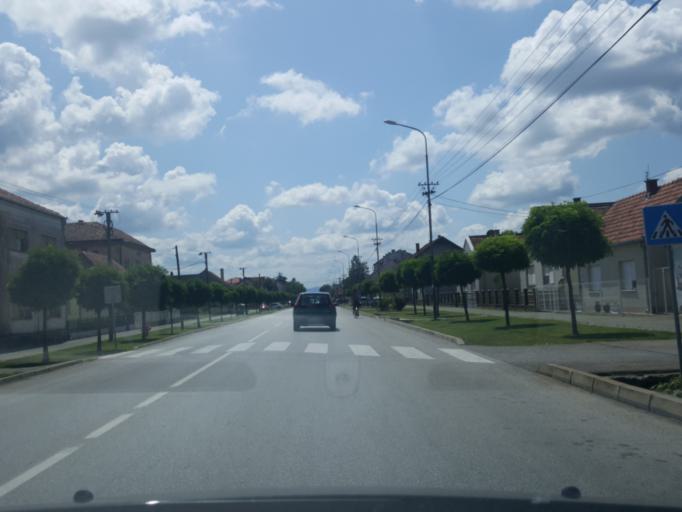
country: RS
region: Central Serbia
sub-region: Macvanski Okrug
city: Bogatic
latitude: 44.8398
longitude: 19.4810
